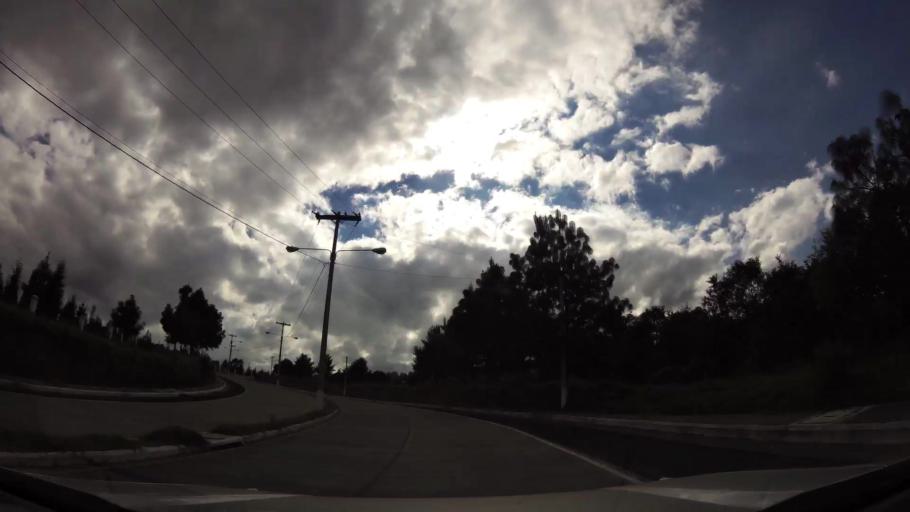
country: GT
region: Quetzaltenango
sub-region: Municipio de La Esperanza
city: La Esperanza
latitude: 14.8381
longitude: -91.5560
